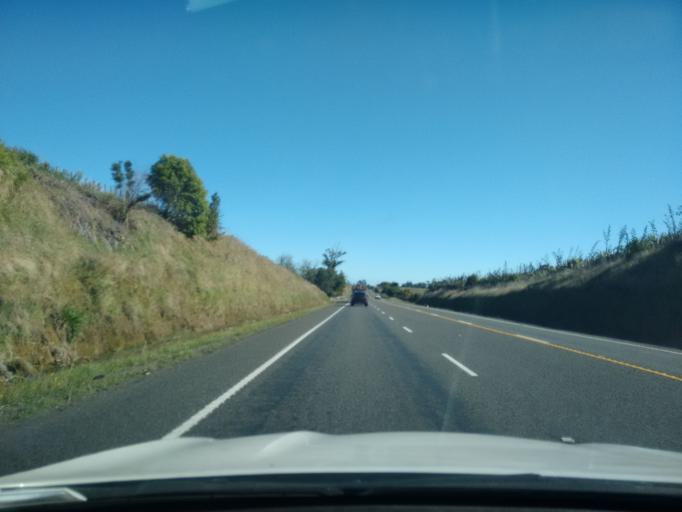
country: NZ
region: Taranaki
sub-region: New Plymouth District
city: New Plymouth
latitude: -39.1387
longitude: 174.1328
